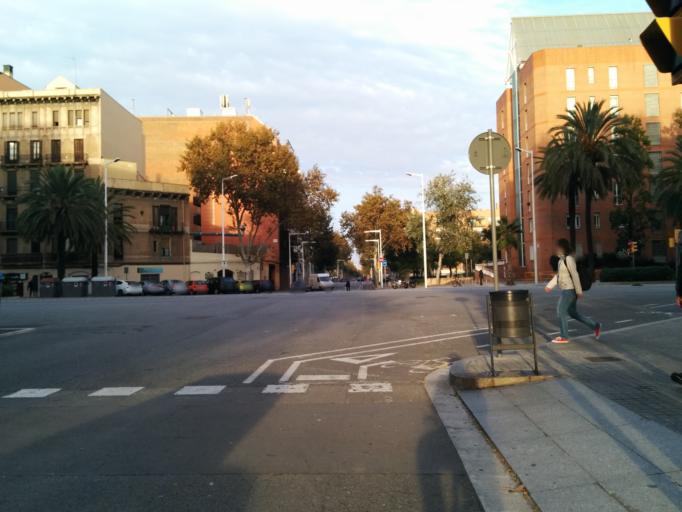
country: ES
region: Catalonia
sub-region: Provincia de Barcelona
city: Ciutat Vella
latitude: 41.3910
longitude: 2.1910
